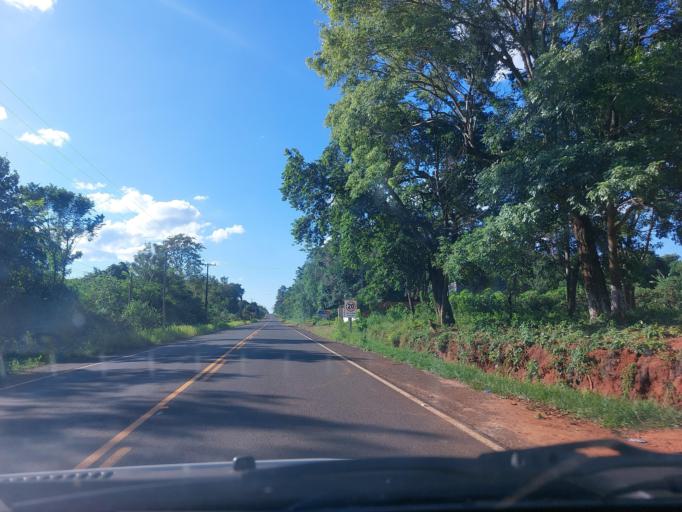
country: PY
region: San Pedro
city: Guayaybi
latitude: -24.5891
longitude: -56.5196
